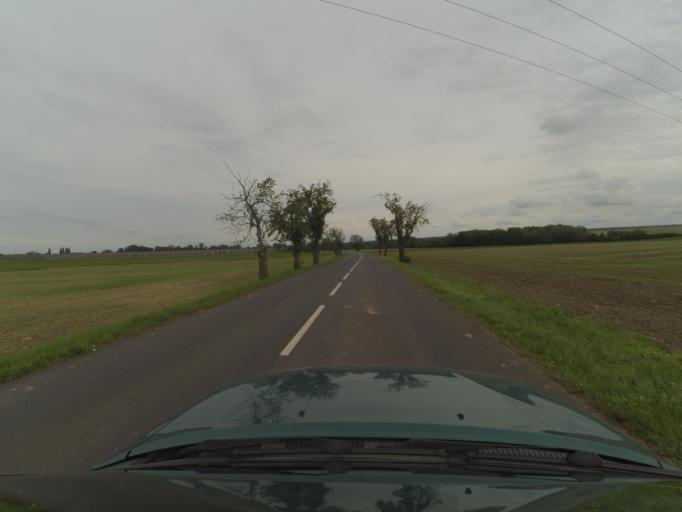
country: CZ
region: Ustecky
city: Cerncice
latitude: 50.3733
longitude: 13.8682
